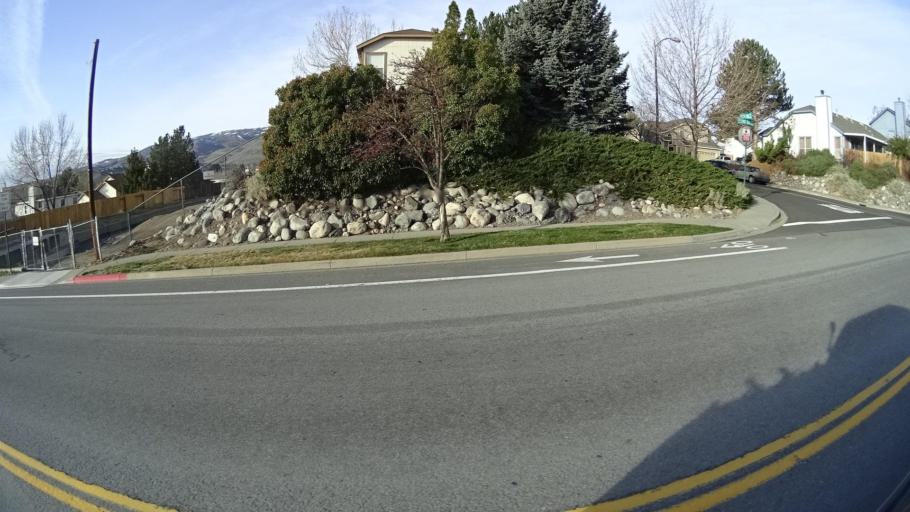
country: US
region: Nevada
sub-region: Washoe County
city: Reno
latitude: 39.5191
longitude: -119.8551
